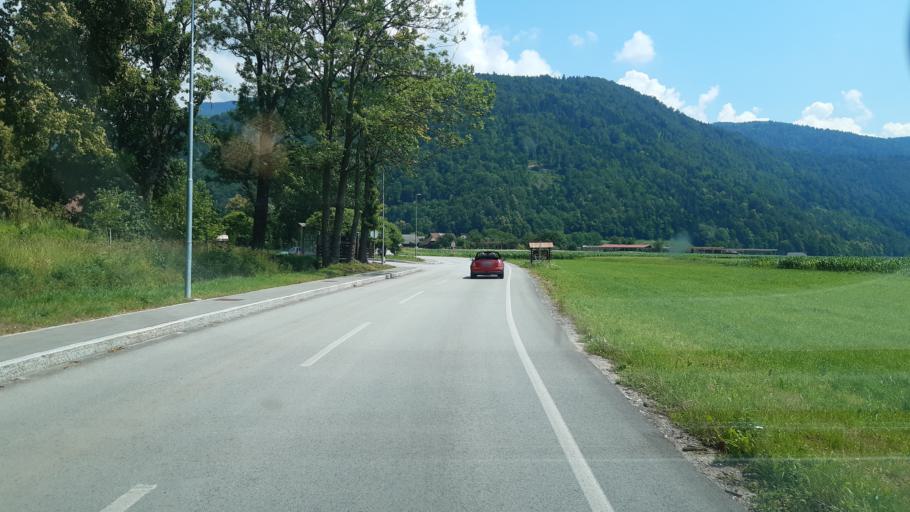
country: SI
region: Cerklje na Gorenjskem
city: Cerklje na Gorenjskem
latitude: 46.2586
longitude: 14.4897
